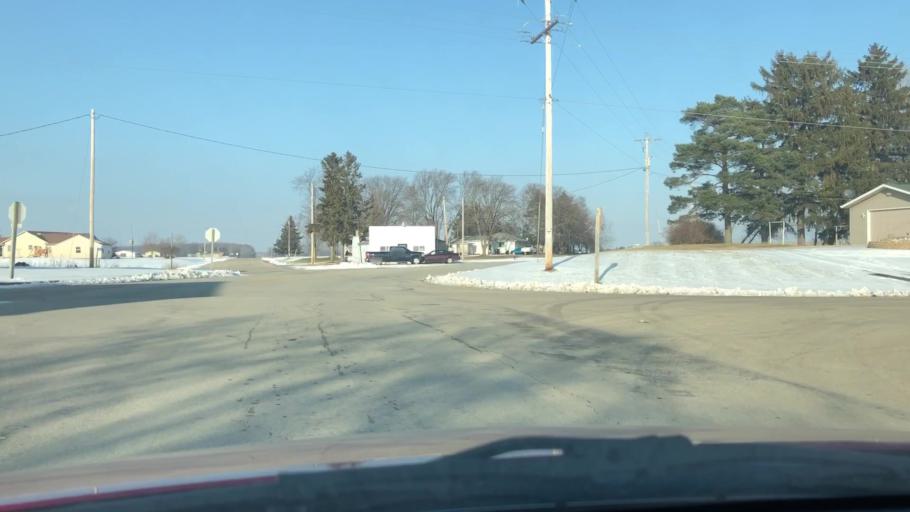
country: US
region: Wisconsin
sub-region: Outagamie County
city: Black Creek
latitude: 44.4146
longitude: -88.3743
